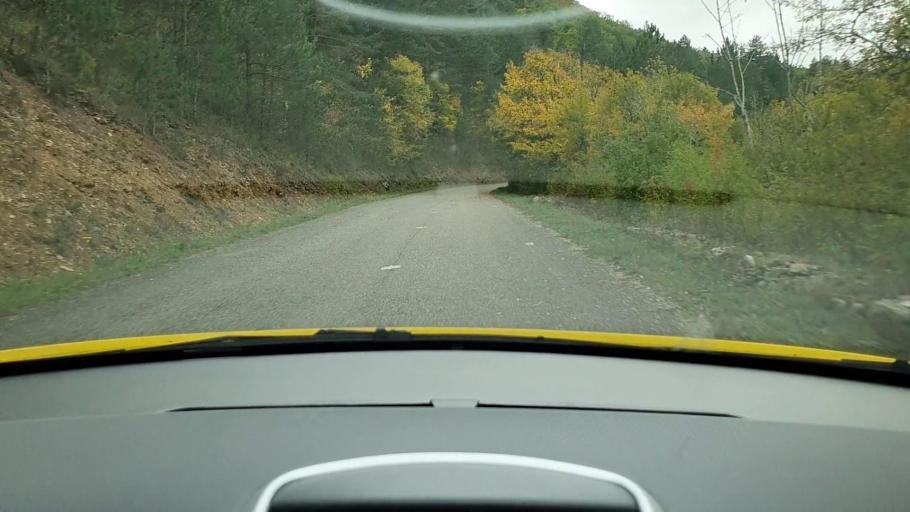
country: FR
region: Languedoc-Roussillon
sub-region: Departement de la Lozere
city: Meyrueis
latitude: 44.0756
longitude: 3.3497
